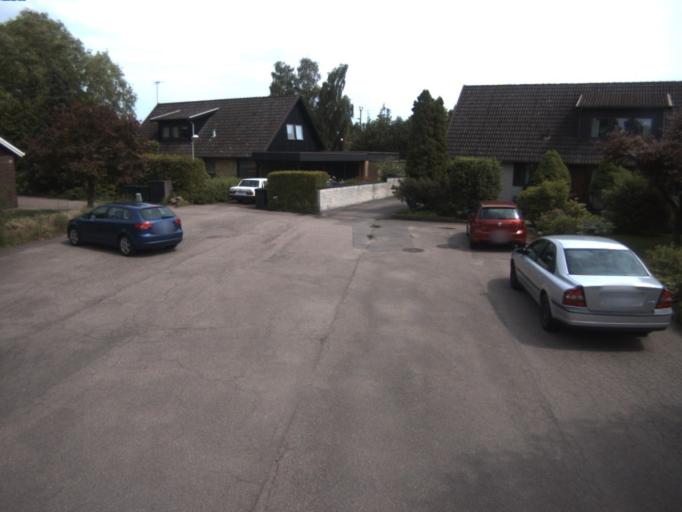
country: SE
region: Skane
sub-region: Helsingborg
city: Odakra
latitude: 56.1106
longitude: 12.7493
